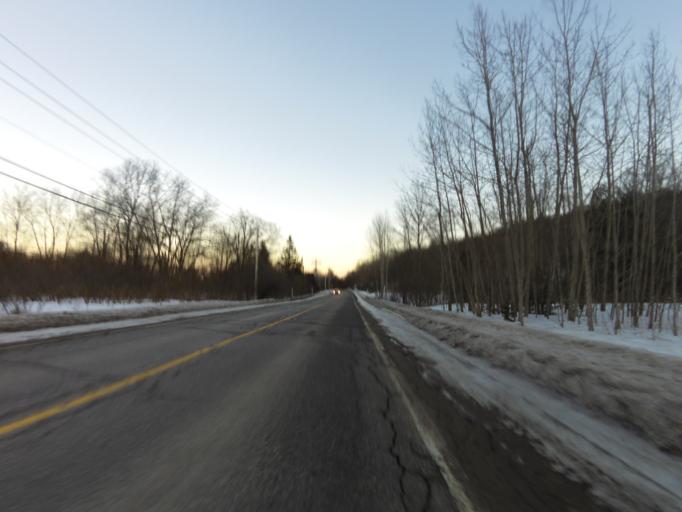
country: CA
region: Quebec
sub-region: Outaouais
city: Gatineau
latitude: 45.4815
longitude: -75.8008
